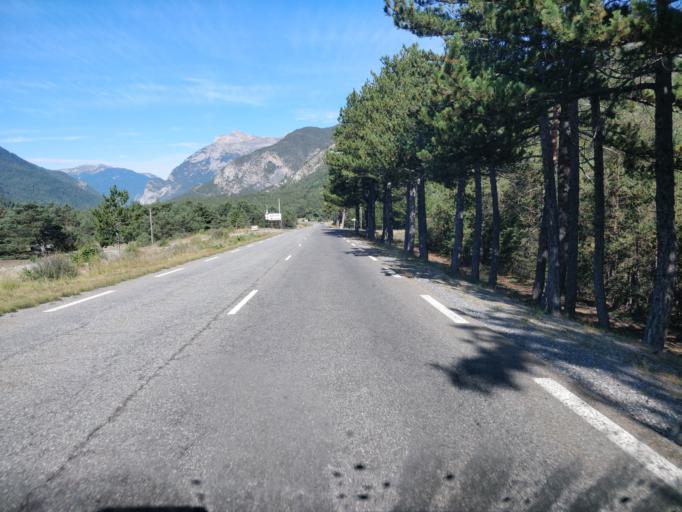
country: FR
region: Provence-Alpes-Cote d'Azur
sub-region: Departement des Alpes-de-Haute-Provence
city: Barcelonnette
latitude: 44.3889
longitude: 6.5949
